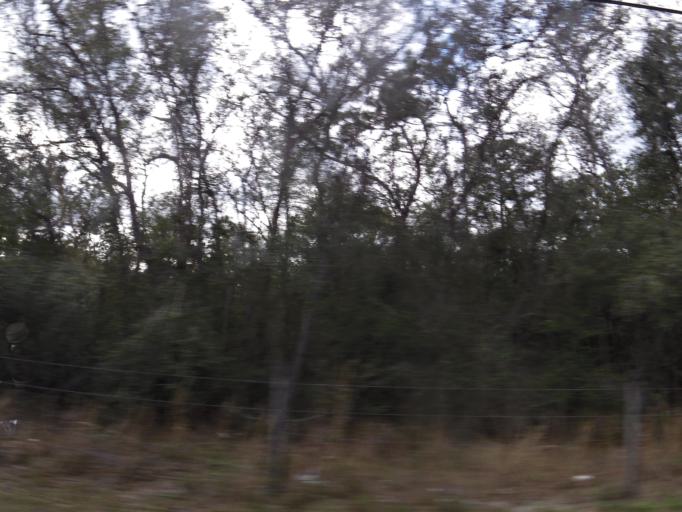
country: US
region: Florida
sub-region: Volusia County
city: Orange City
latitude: 28.9588
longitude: -81.2659
